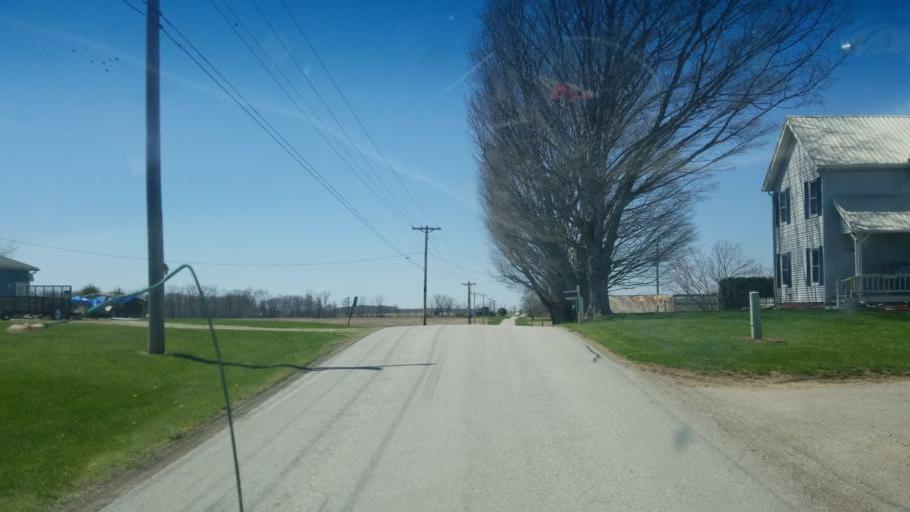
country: US
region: Ohio
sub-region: Huron County
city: Greenwich
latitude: 41.0938
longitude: -82.4923
